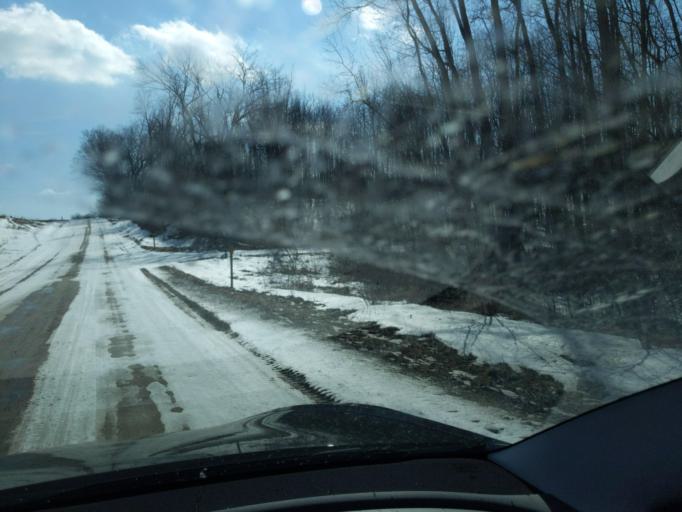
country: US
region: Michigan
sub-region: Livingston County
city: Fowlerville
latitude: 42.5372
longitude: -84.0882
